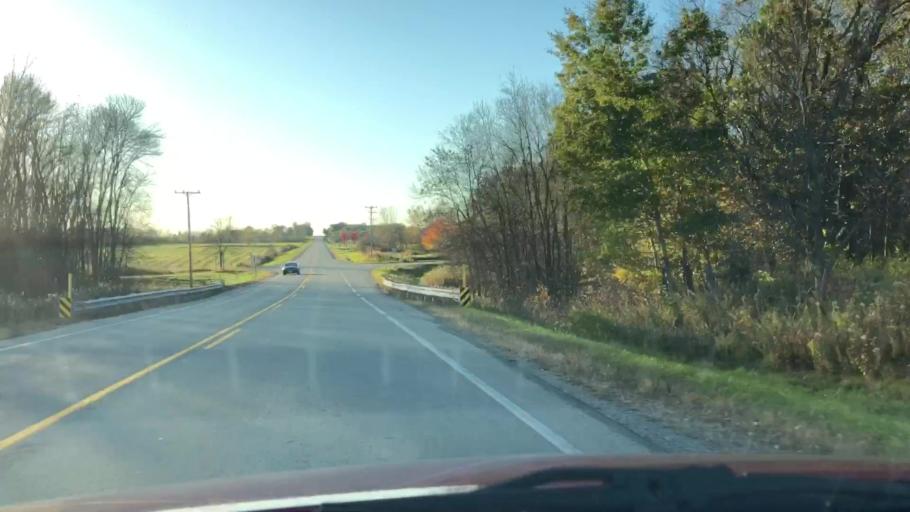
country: US
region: Wisconsin
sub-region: Brown County
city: Oneida
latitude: 44.4444
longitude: -88.2496
